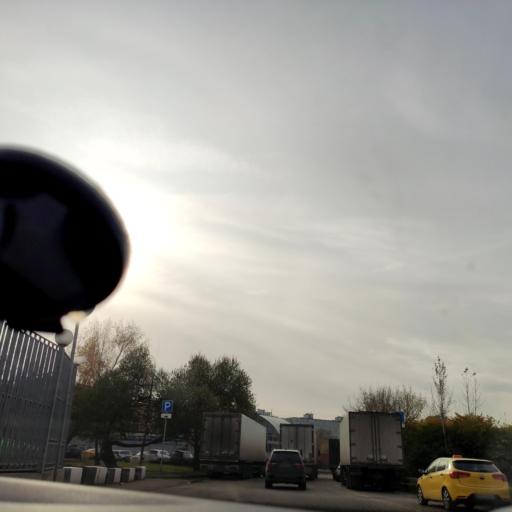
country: RU
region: Moskovskaya
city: Vostochnoe Degunino
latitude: 55.8842
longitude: 37.5529
